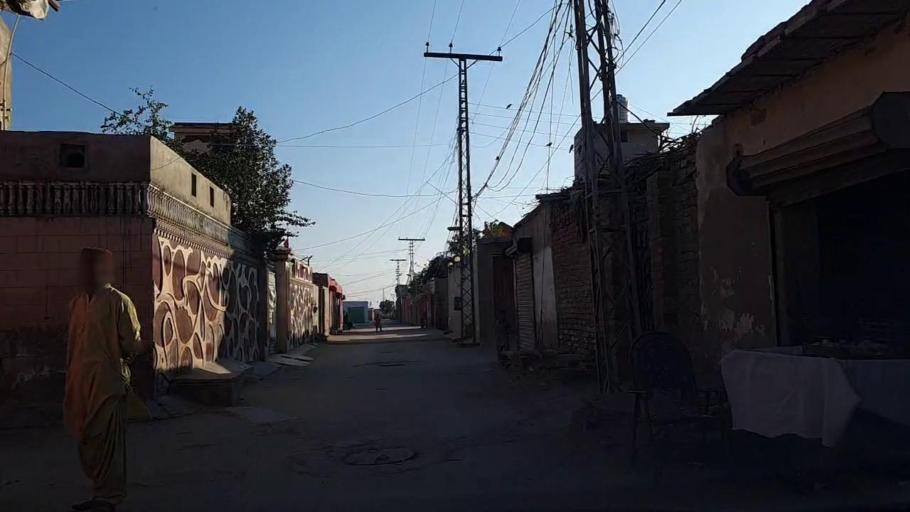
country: PK
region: Sindh
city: Nawabshah
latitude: 26.2258
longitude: 68.3613
